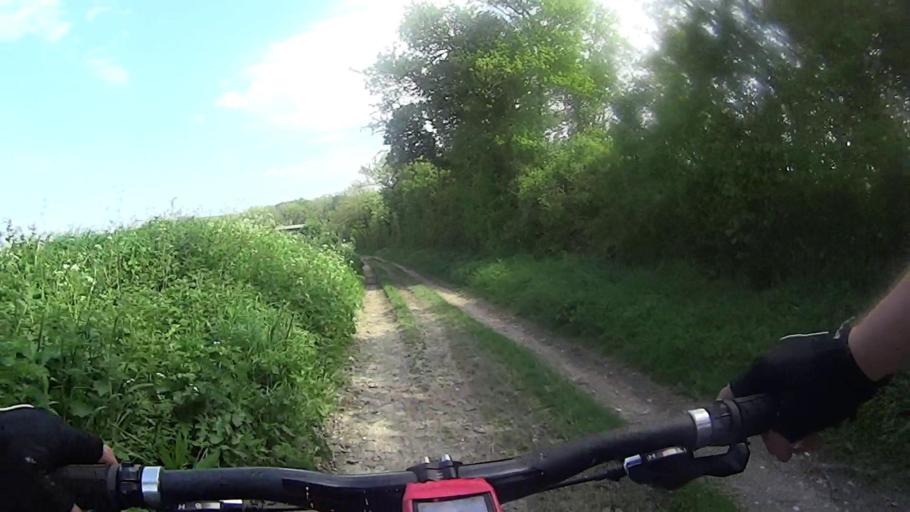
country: GB
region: England
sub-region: Hampshire
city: Petersfield
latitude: 50.9644
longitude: -0.8990
